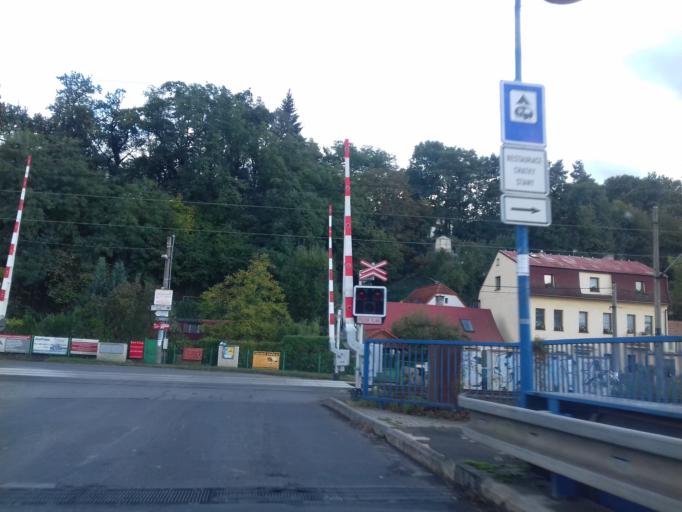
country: CZ
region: Central Bohemia
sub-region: Okres Praha-Zapad
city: Dobrichovice
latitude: 49.9251
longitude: 14.2767
